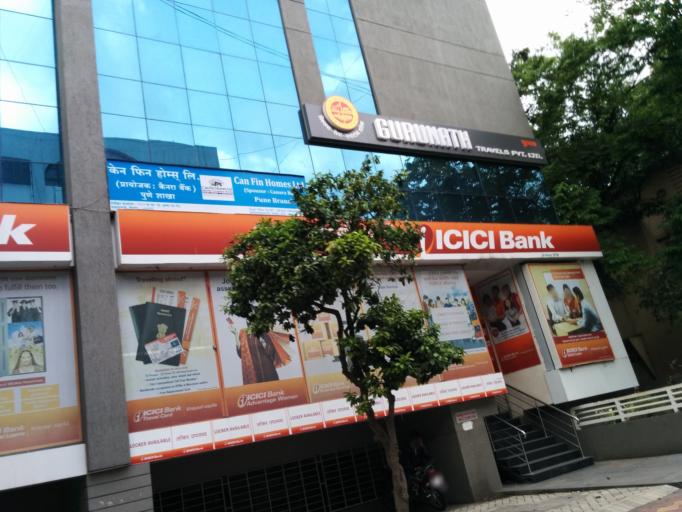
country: IN
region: Maharashtra
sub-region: Pune Division
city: Pune
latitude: 18.5070
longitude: 73.8513
